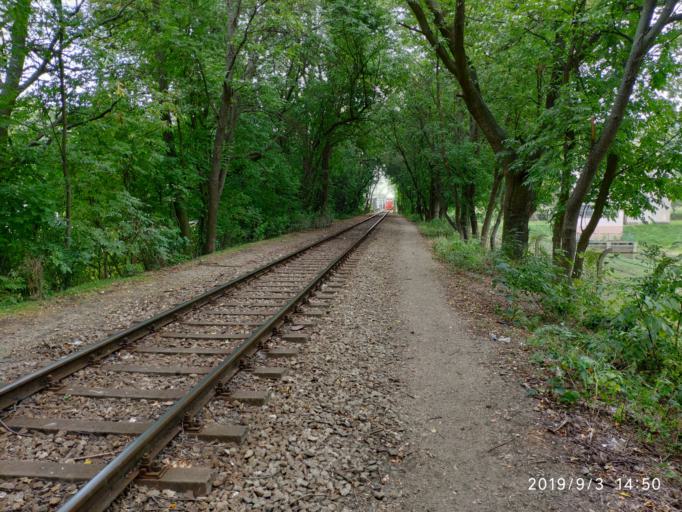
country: PL
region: Lubusz
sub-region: Powiat nowosolski
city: Nowa Sol
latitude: 51.7954
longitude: 15.7201
